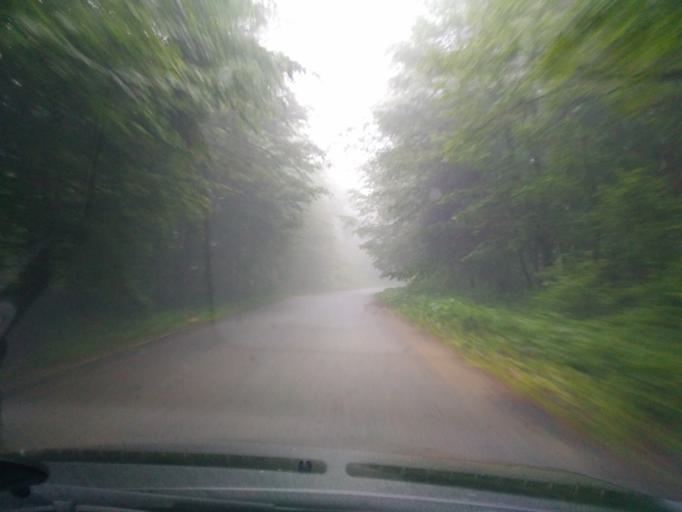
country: PL
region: Subcarpathian Voivodeship
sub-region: Powiat debicki
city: Debica
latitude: 49.9751
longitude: 21.3978
